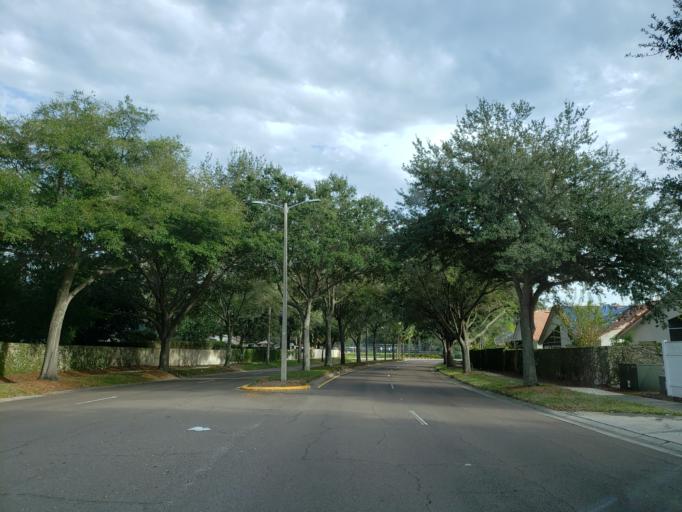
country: US
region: Florida
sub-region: Hillsborough County
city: Bloomingdale
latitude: 27.8849
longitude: -82.2665
